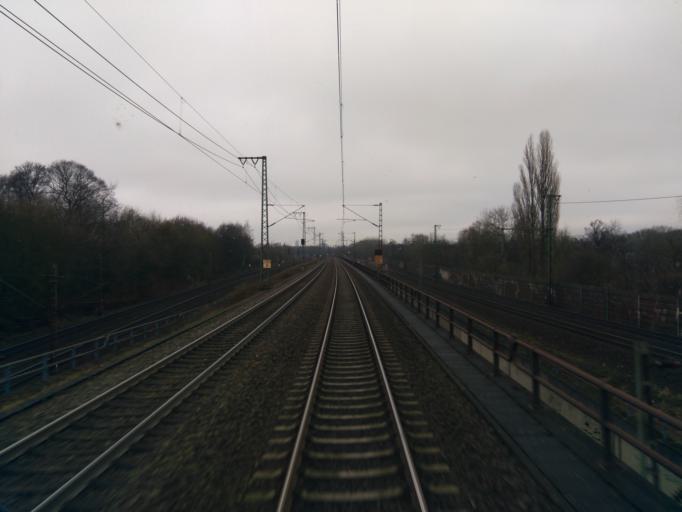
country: DE
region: Hamburg
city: Harburg
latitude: 53.4380
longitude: 10.0136
